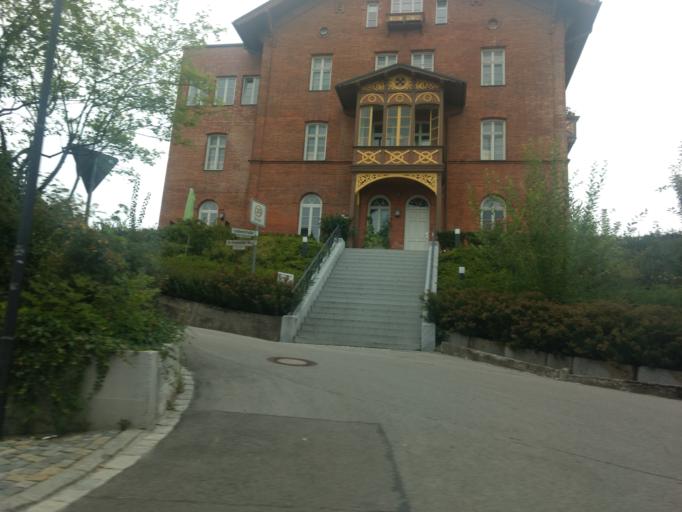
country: DE
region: Bavaria
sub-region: Lower Bavaria
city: Simbach am Inn
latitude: 48.2689
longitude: 13.0300
